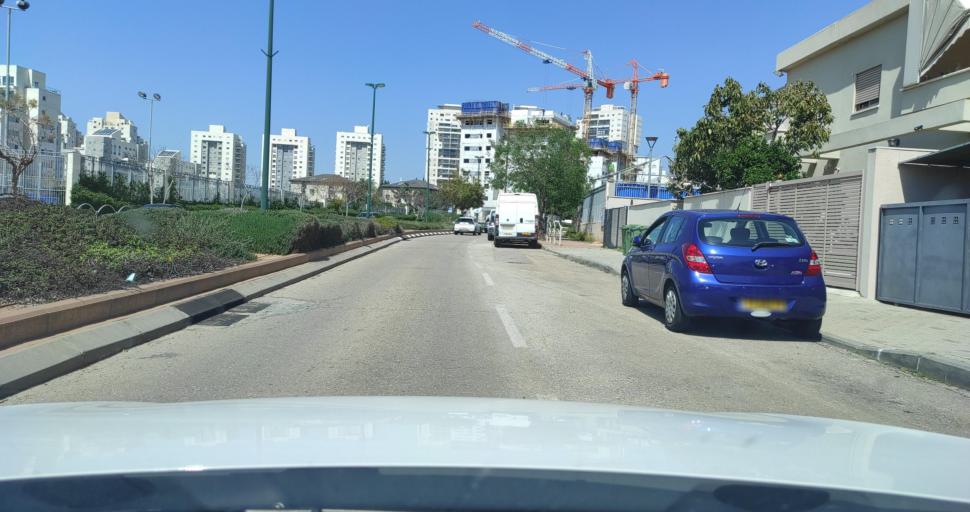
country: IL
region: Central District
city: Nordiyya
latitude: 32.2984
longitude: 34.8780
